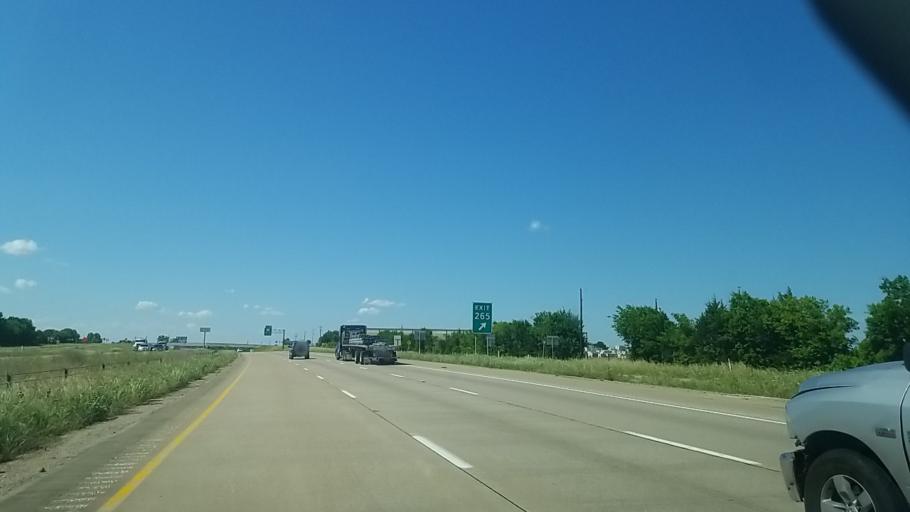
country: US
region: Texas
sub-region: Ellis County
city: Ferris
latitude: 32.5098
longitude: -96.6633
